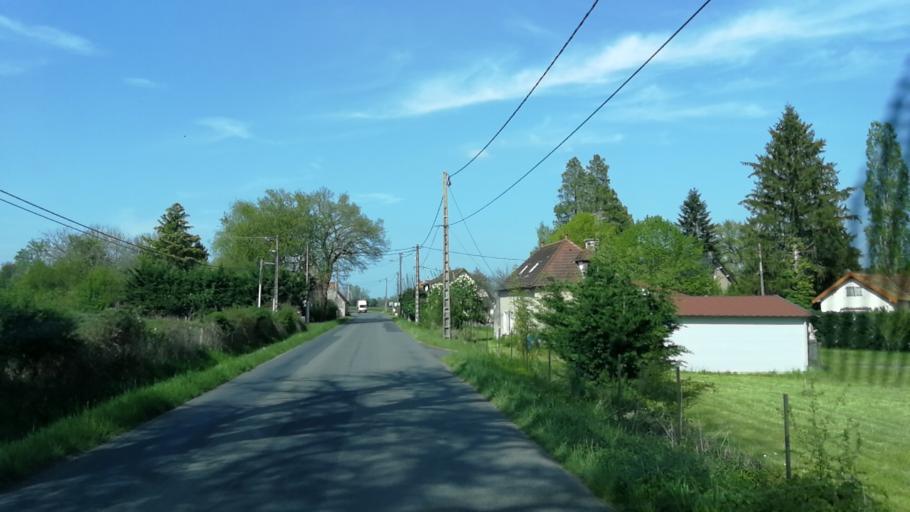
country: FR
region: Auvergne
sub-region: Departement de l'Allier
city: Saint-Gerand-le-Puy
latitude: 46.3739
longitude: 3.5819
